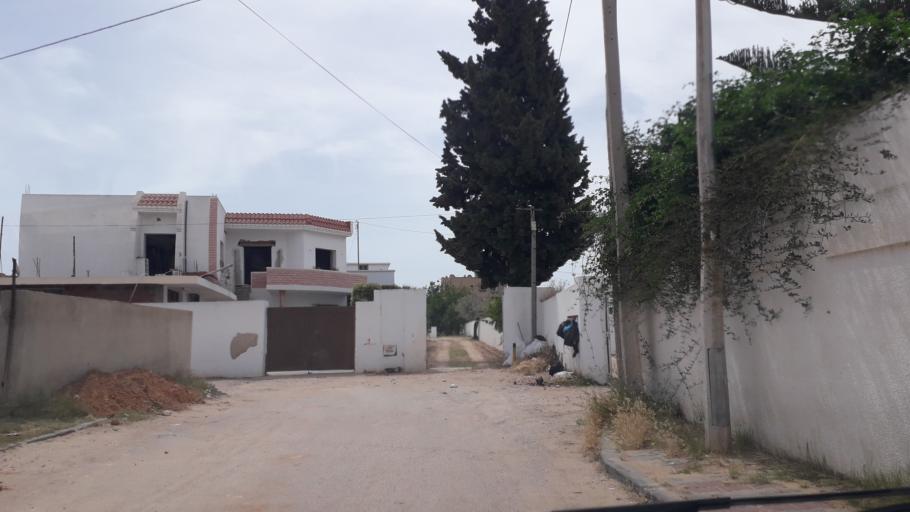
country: TN
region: Safaqis
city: Al Qarmadah
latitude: 34.8034
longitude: 10.7642
